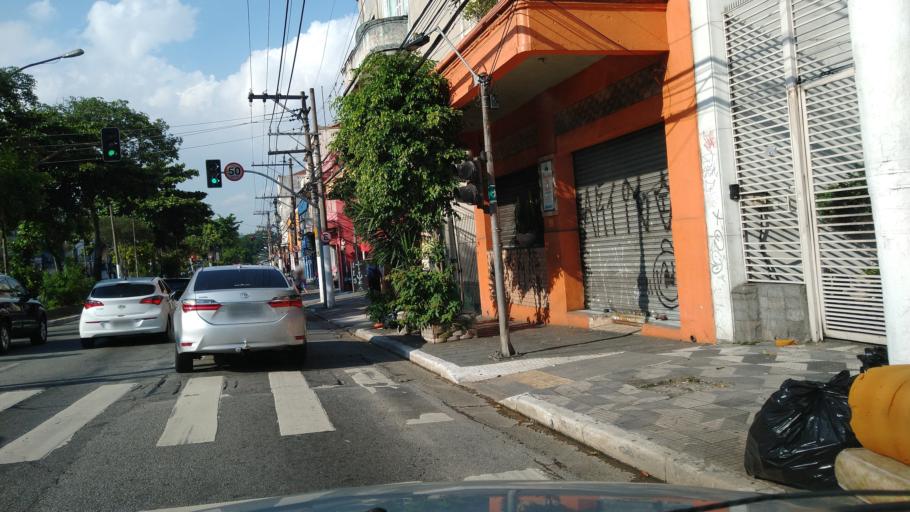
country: BR
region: Sao Paulo
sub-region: Sao Paulo
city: Sao Paulo
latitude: -23.5569
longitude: -46.6001
